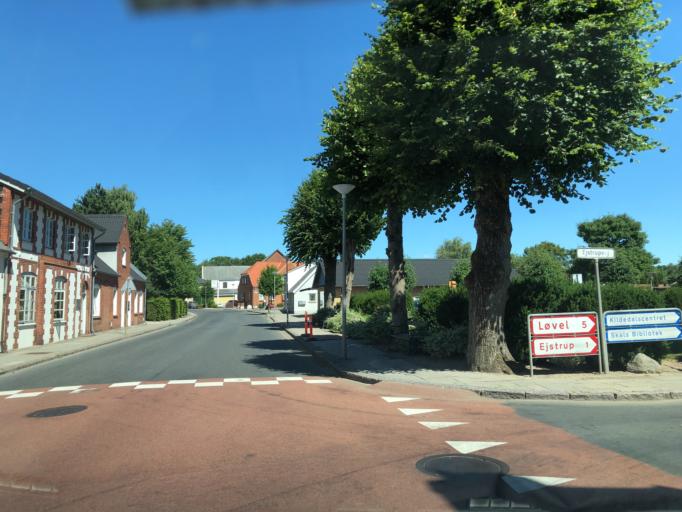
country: DK
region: Central Jutland
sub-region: Viborg Kommune
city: Viborg
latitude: 56.5579
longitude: 9.4035
